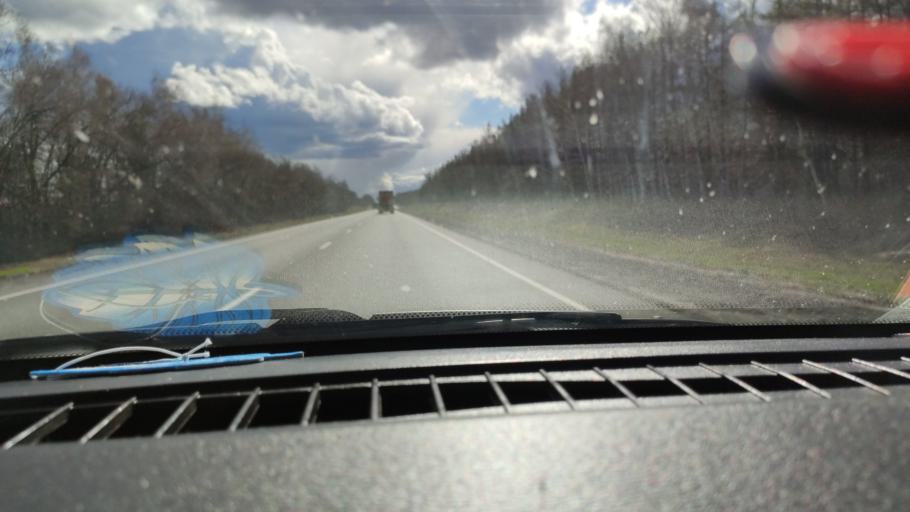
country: RU
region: Saratov
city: Khvalynsk
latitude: 52.5678
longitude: 48.0981
